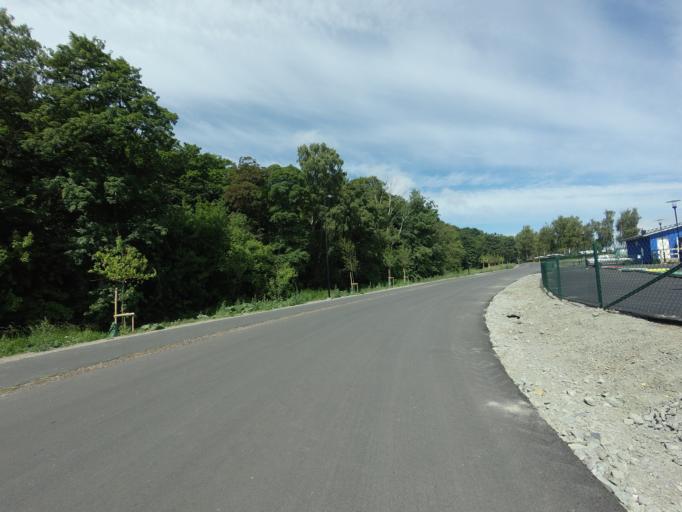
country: SE
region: Skane
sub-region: Simrishamns Kommun
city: Simrishamn
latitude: 55.5667
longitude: 14.3373
